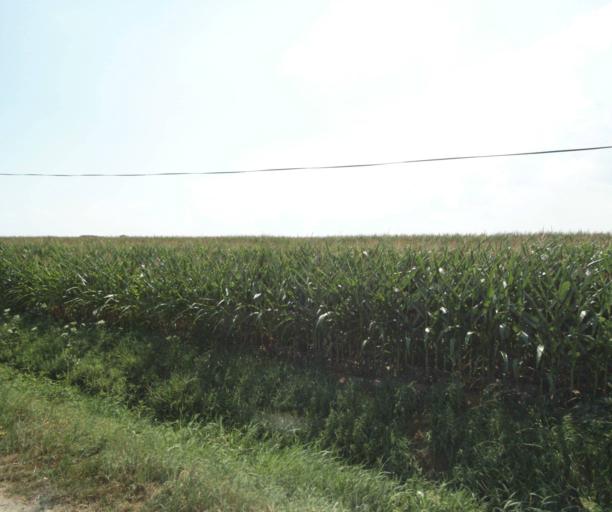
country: FR
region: Nord-Pas-de-Calais
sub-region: Departement du Nord
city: Comines
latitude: 50.7429
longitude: 3.0042
